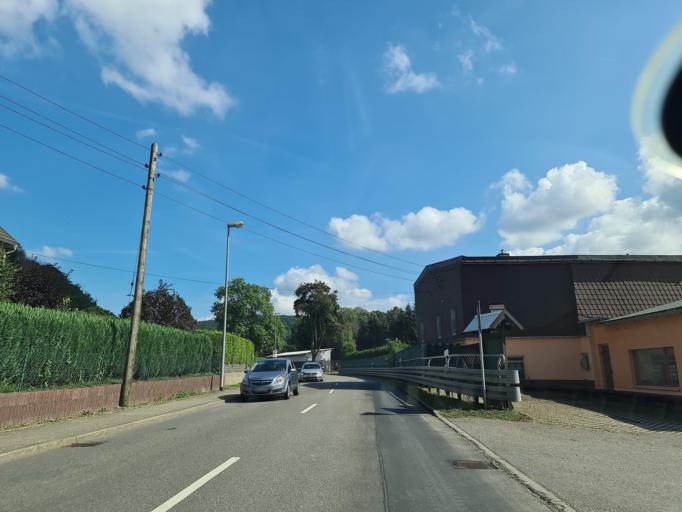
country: DE
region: Saxony
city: Heidersdorf
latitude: 50.6473
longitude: 13.3833
